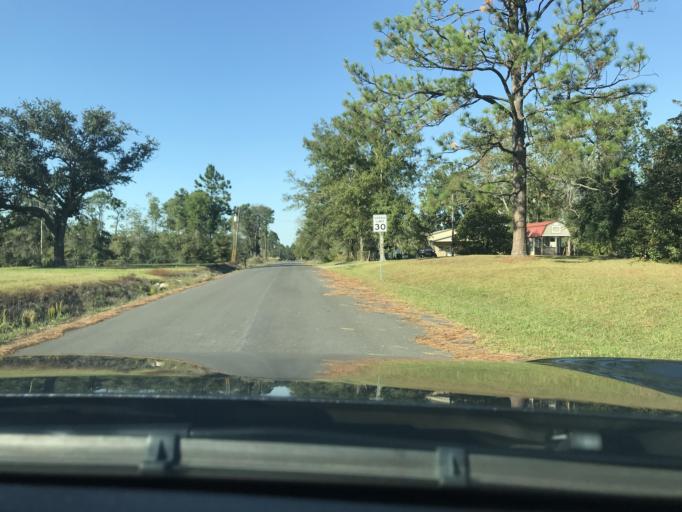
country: US
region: Louisiana
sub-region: Calcasieu Parish
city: Westlake
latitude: 30.3155
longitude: -93.2688
